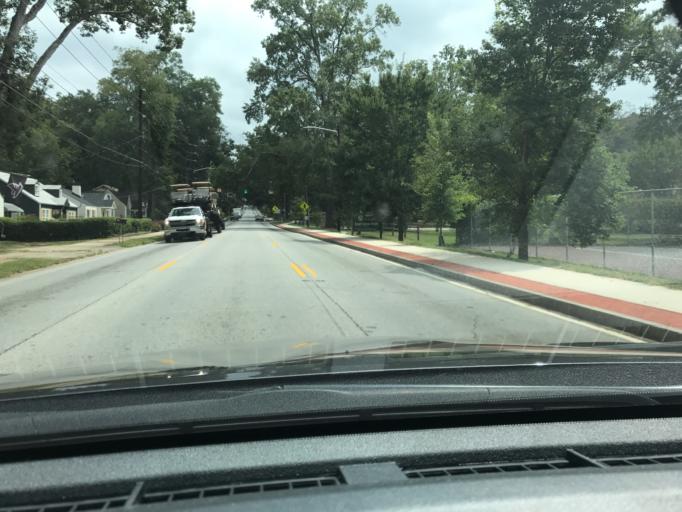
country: US
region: Georgia
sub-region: DeKalb County
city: Decatur
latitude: 33.7471
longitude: -84.3007
